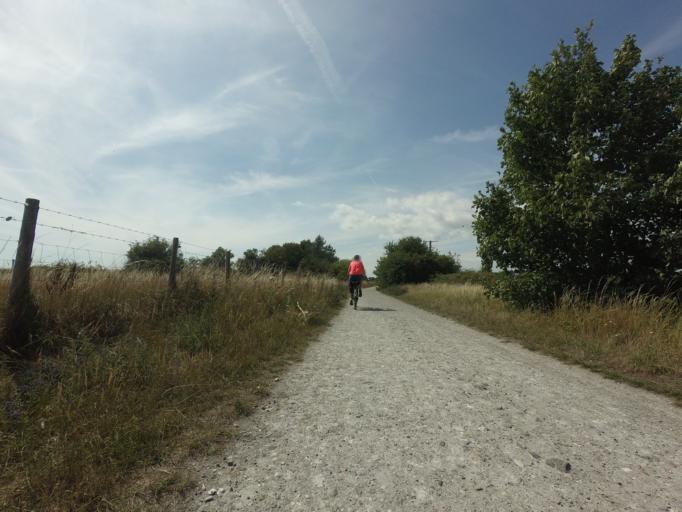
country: GB
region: England
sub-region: East Sussex
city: Rye
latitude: 50.9490
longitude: 0.7498
